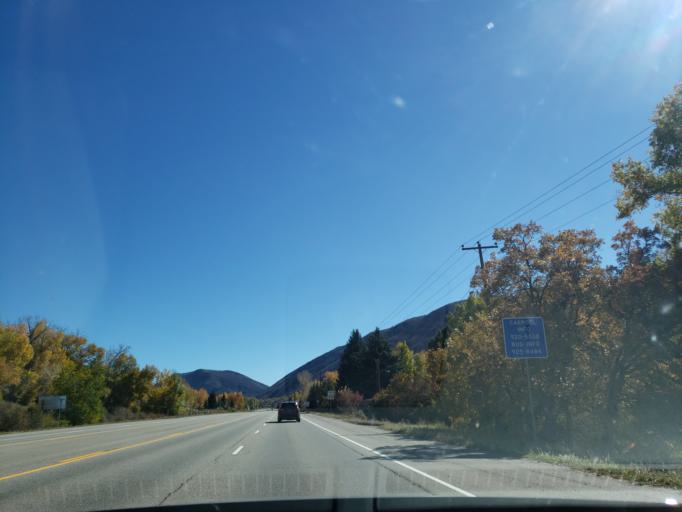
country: US
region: Colorado
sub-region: Eagle County
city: Basalt
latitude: 39.3569
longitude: -107.0244
